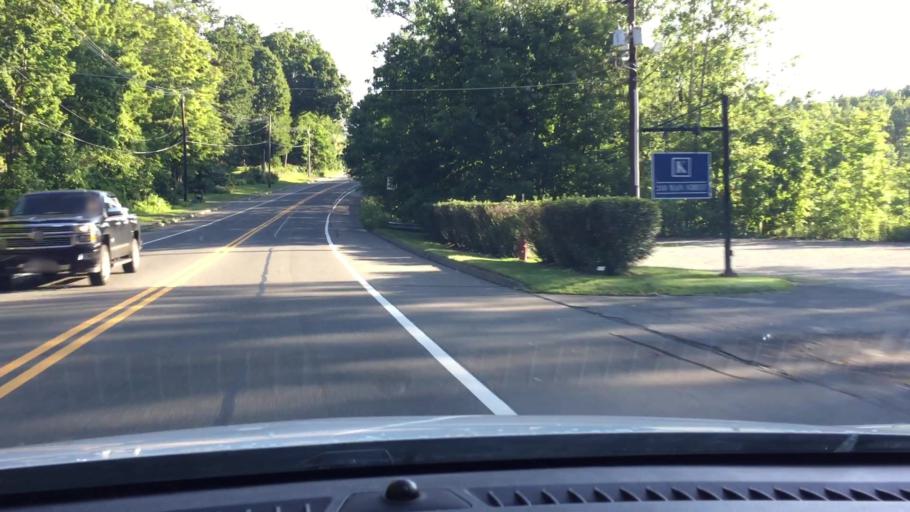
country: US
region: Massachusetts
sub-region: Berkshire County
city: Lenox
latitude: 42.3677
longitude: -73.2813
